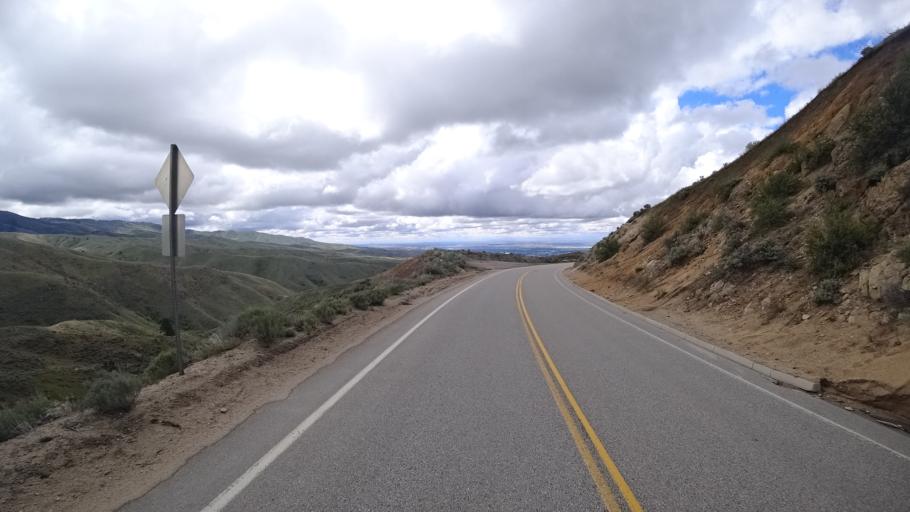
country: US
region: Idaho
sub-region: Ada County
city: Boise
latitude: 43.7165
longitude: -116.1619
